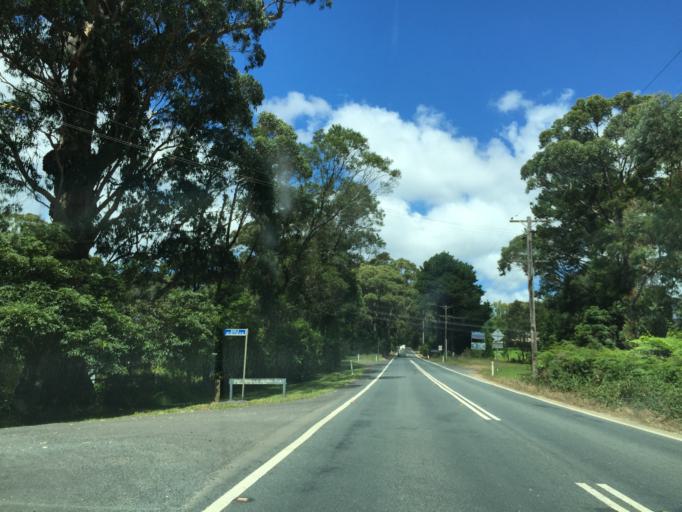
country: AU
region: New South Wales
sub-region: Blue Mountains Municipality
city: Lawson
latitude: -33.5227
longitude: 150.4605
